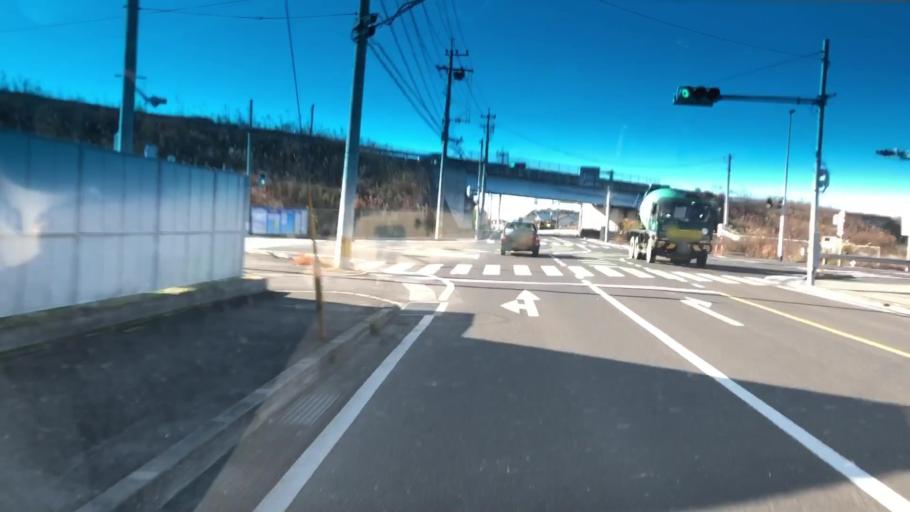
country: JP
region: Kagoshima
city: Satsumasendai
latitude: 31.8214
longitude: 130.2610
